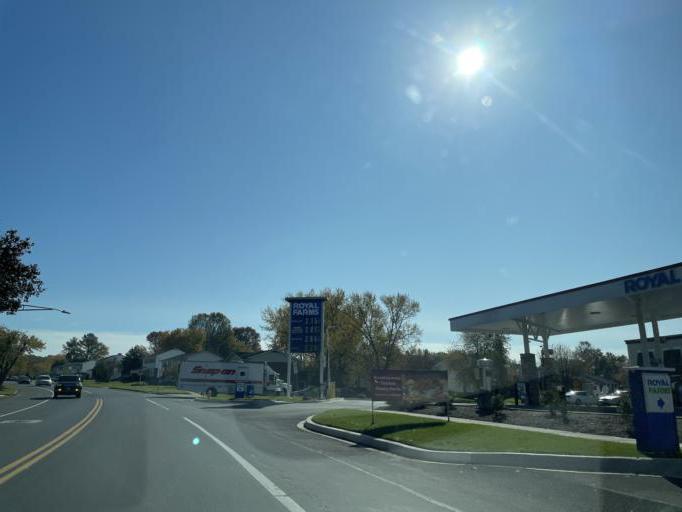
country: US
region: Maryland
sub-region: Harford County
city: Joppatowne
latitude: 39.4083
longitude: -76.3490
